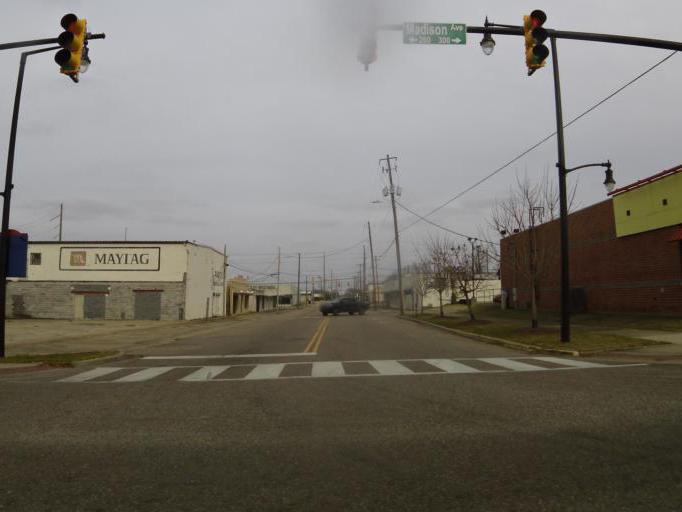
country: US
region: Alabama
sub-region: Montgomery County
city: Montgomery
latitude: 32.3800
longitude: -86.3051
